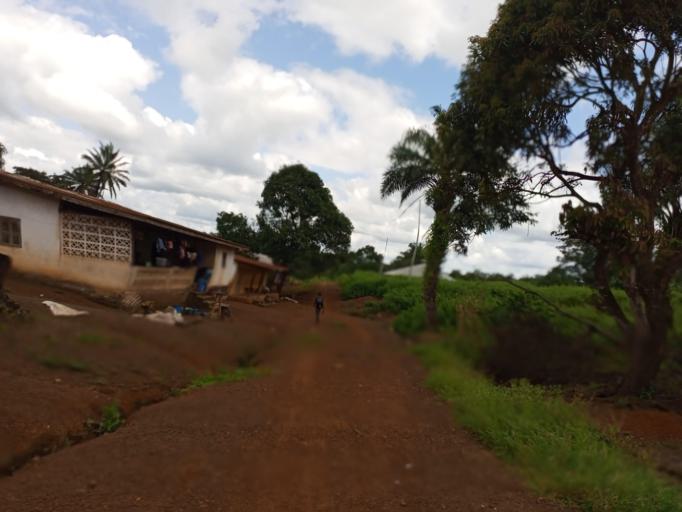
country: SL
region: Northern Province
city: Kamakwie
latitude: 9.4962
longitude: -12.2345
